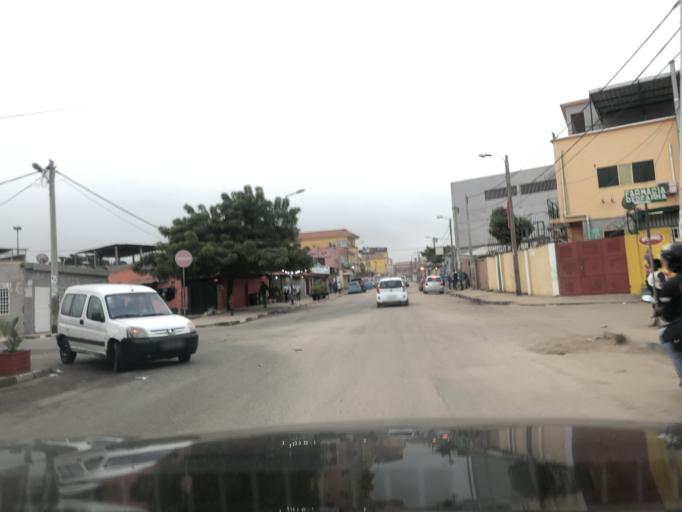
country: AO
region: Luanda
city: Luanda
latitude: -8.8455
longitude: 13.2246
